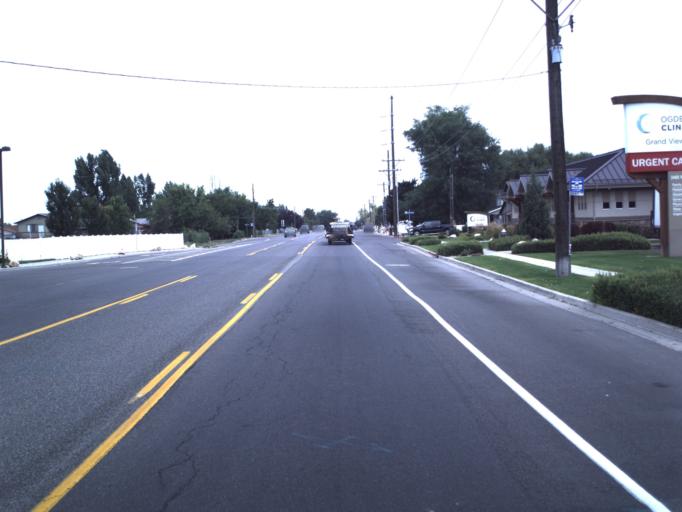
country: US
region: Utah
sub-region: Davis County
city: Clinton
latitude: 41.1679
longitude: -112.0644
